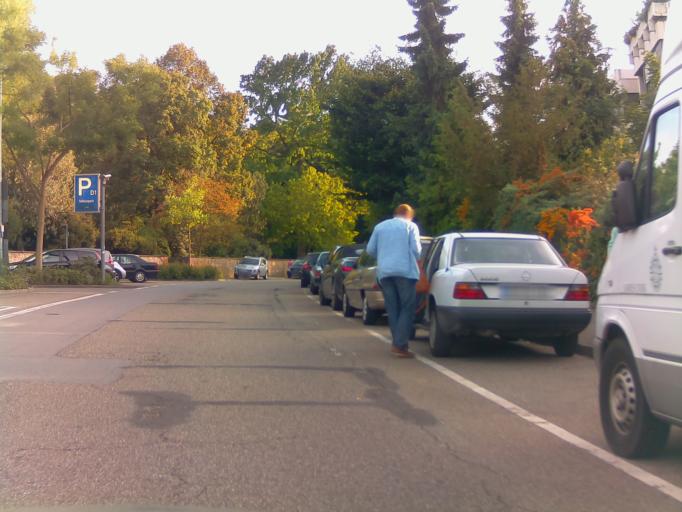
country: DE
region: Baden-Wuerttemberg
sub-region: Karlsruhe Region
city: Weinheim
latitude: 49.5452
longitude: 8.6694
